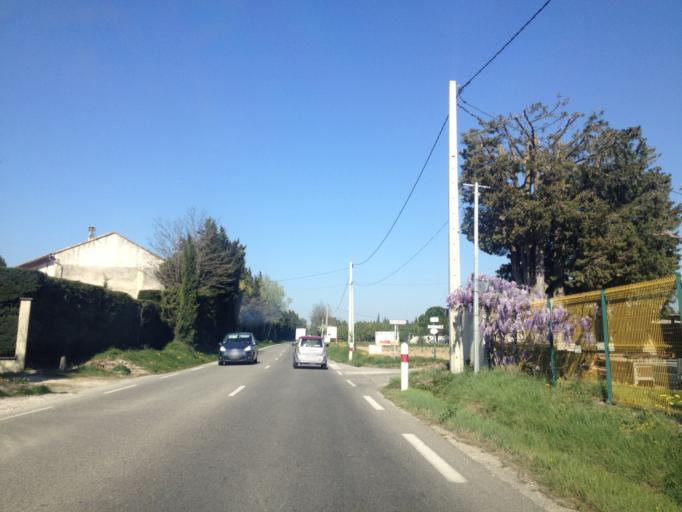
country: FR
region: Provence-Alpes-Cote d'Azur
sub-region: Departement du Vaucluse
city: Sarrians
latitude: 44.1004
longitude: 4.9383
